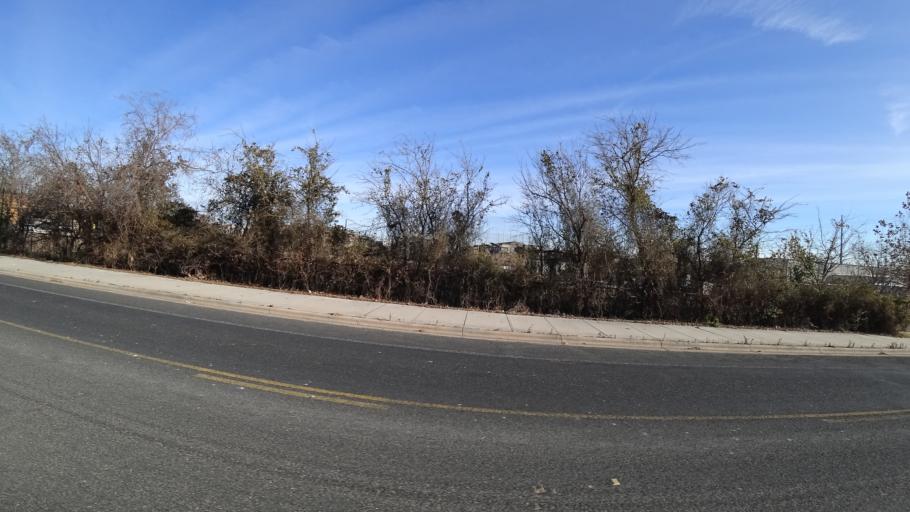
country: US
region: Texas
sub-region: Travis County
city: Wells Branch
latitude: 30.3944
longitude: -97.7187
